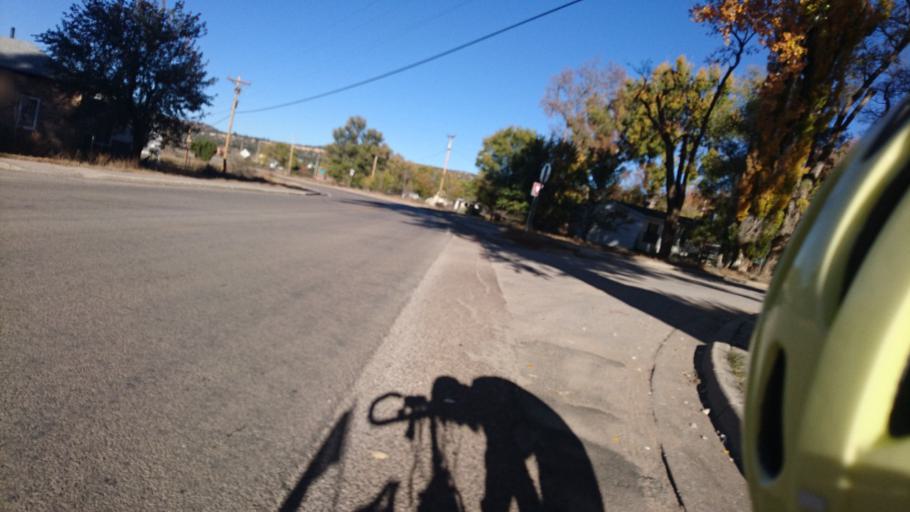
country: US
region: New Mexico
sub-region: McKinley County
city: Black Rock
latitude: 35.1331
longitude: -108.4961
